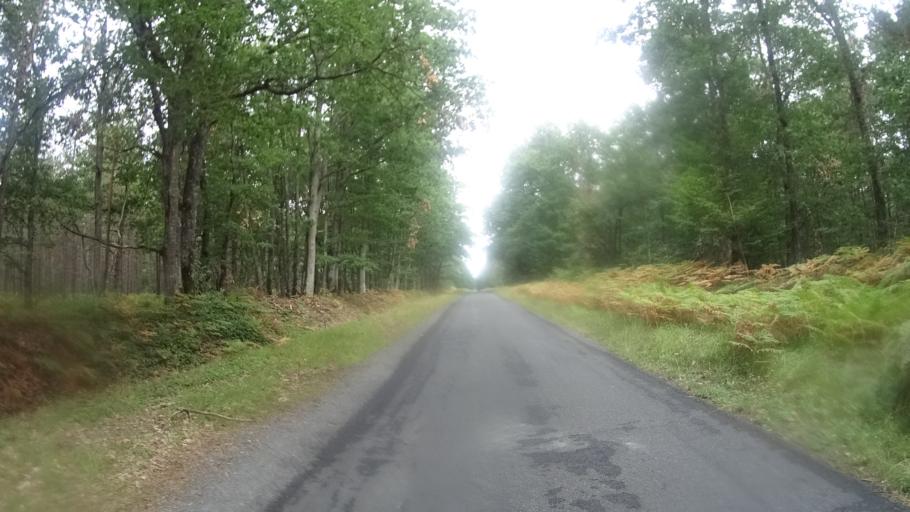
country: FR
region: Centre
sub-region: Departement du Loiret
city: Vitry-aux-Loges
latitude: 48.0335
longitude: 2.2583
